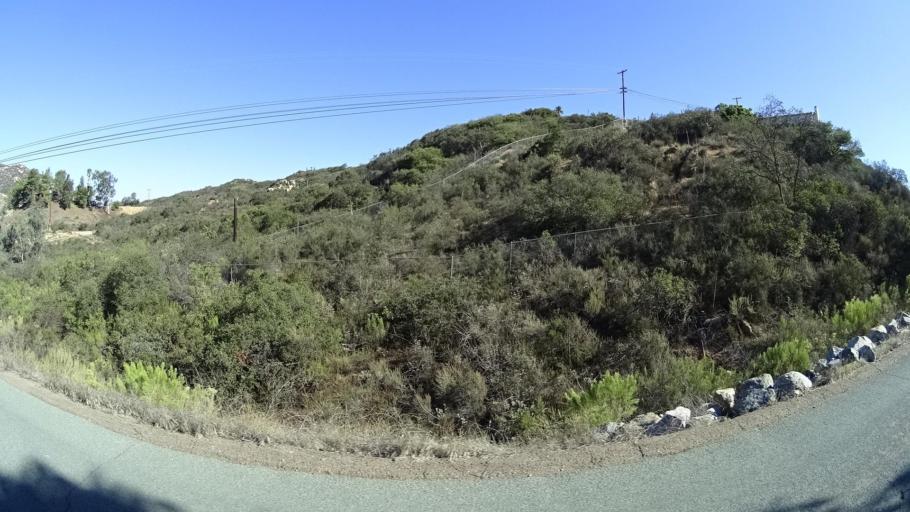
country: US
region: California
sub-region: San Diego County
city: Jamul
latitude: 32.7294
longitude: -116.8289
